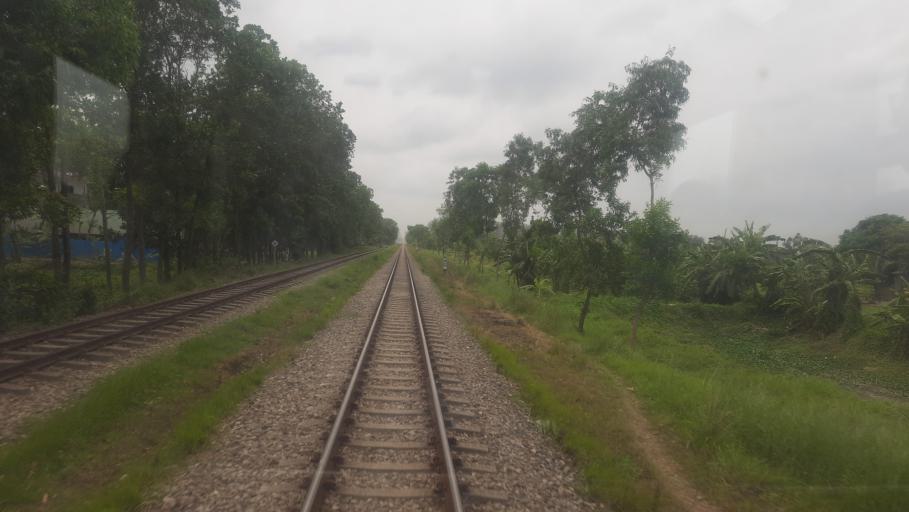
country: BD
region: Chittagong
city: Feni
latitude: 23.0299
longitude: 91.3800
